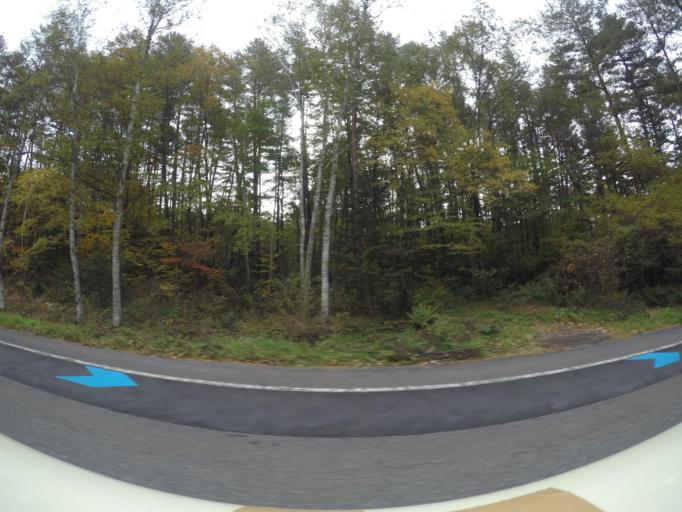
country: JP
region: Nagano
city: Ina
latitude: 35.9372
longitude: 137.6299
